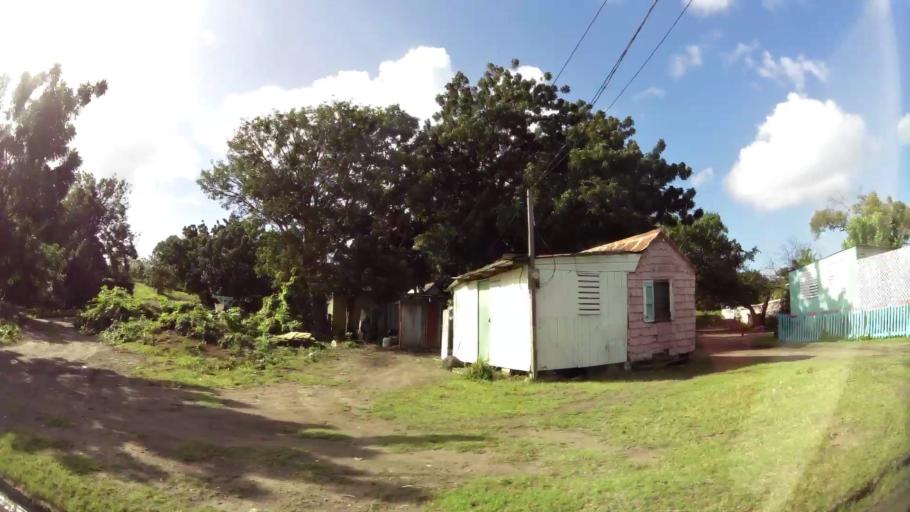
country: KN
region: Saint Paul Charlestown
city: Charlestown
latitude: 17.1325
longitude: -62.6282
